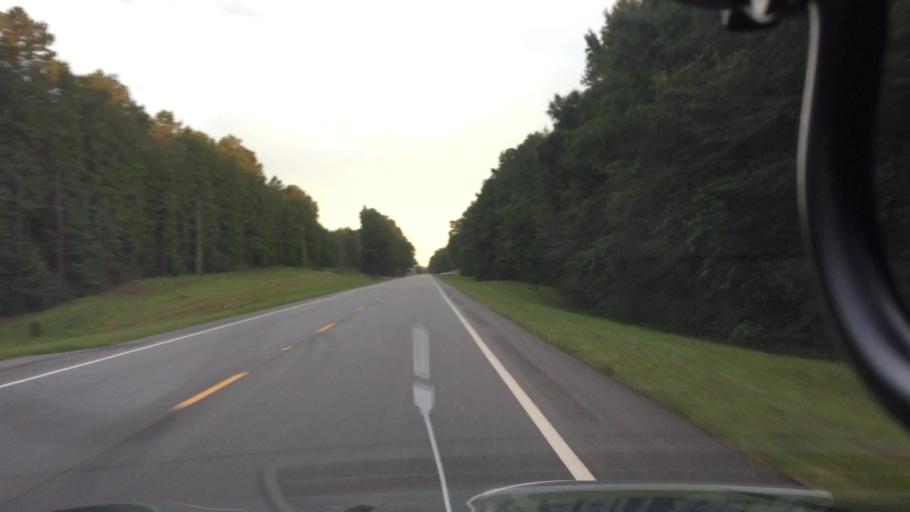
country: US
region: Alabama
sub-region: Coffee County
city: New Brockton
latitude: 31.5082
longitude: -85.9161
